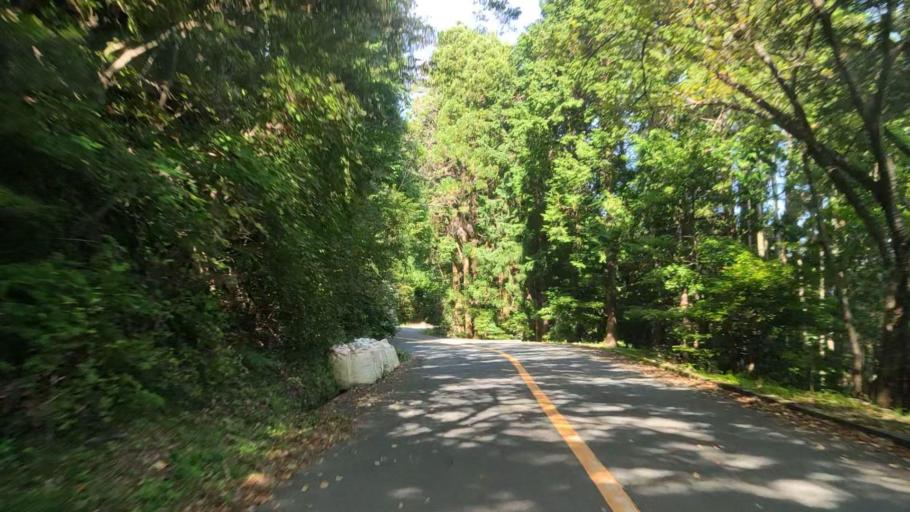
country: JP
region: Shizuoka
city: Shizuoka-shi
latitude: 34.9784
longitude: 138.4725
